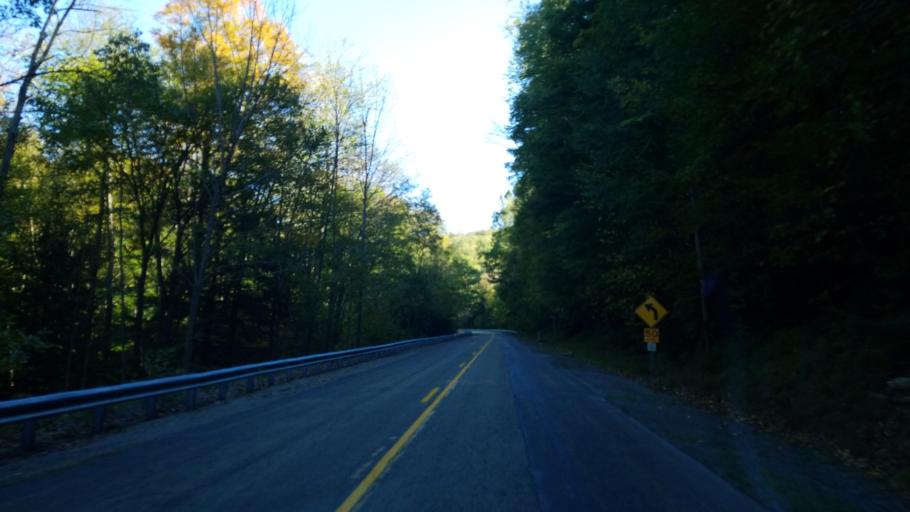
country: US
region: Pennsylvania
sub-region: Clearfield County
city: Shiloh
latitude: 41.2523
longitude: -78.3811
